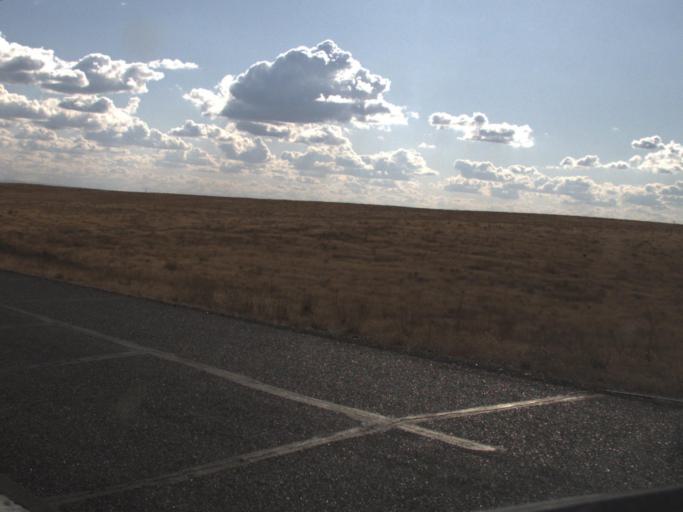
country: US
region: Oregon
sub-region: Umatilla County
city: Umatilla
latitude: 45.9615
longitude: -119.3426
